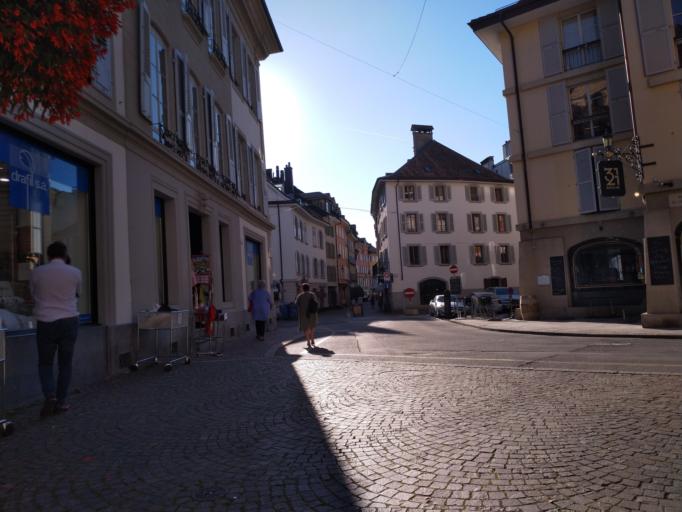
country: CH
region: Vaud
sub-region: Riviera-Pays-d'Enhaut District
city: Vevey
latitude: 46.4589
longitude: 6.8453
